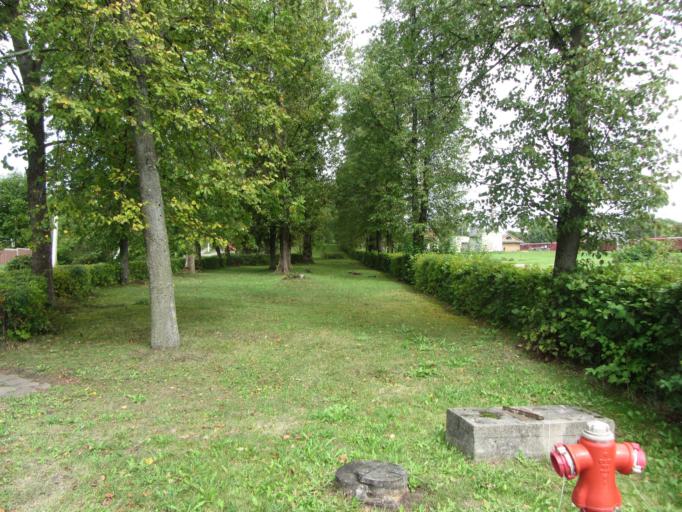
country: LT
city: Dukstas
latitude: 55.5178
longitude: 26.3222
